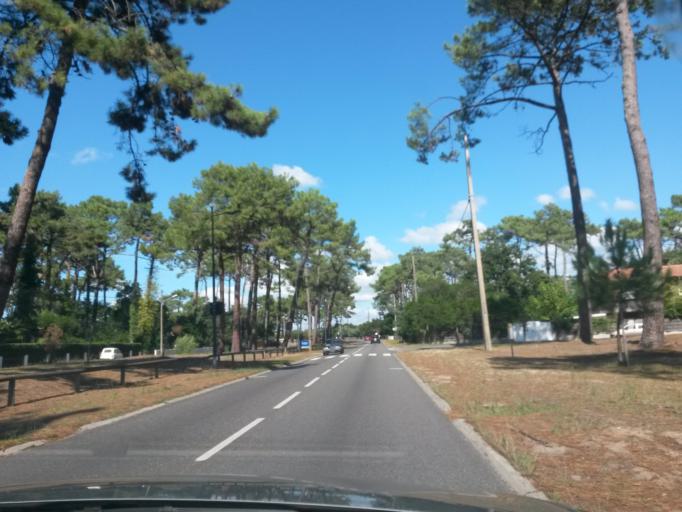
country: FR
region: Aquitaine
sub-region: Departement de la Gironde
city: Arcachon
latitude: 44.7044
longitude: -1.2264
